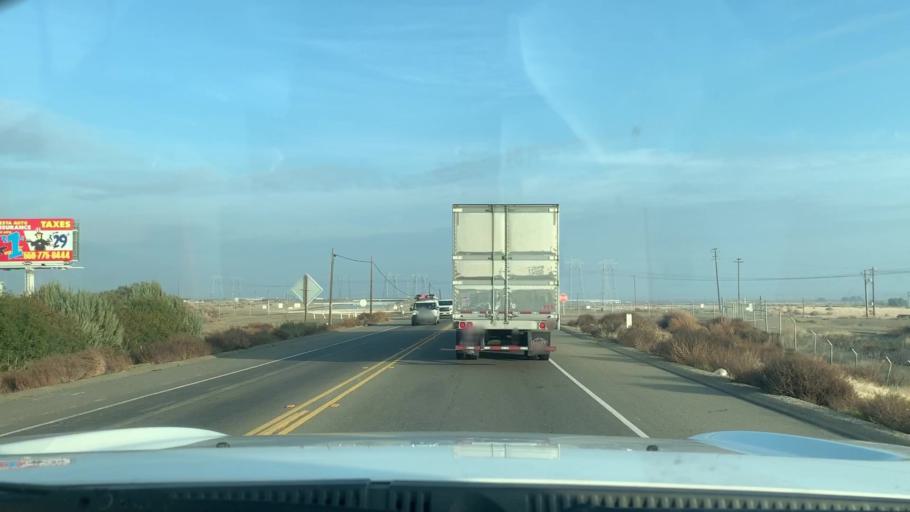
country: US
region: California
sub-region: Kings County
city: Kettleman City
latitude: 35.9909
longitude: -119.9596
